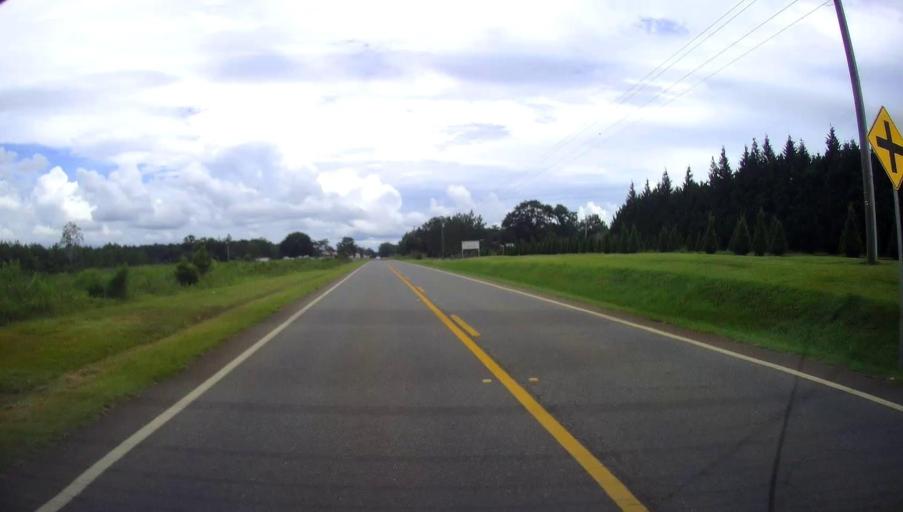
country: US
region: Georgia
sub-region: Schley County
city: Ellaville
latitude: 32.2523
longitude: -84.3355
